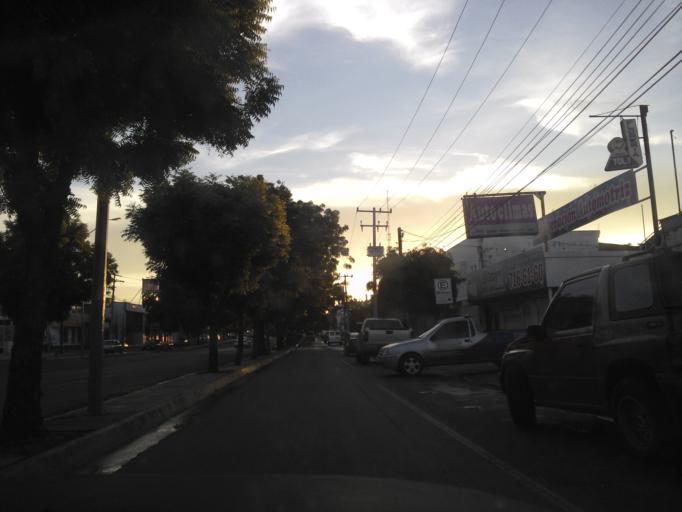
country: MX
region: Sinaloa
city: Culiacan
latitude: 24.7974
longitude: -107.3956
